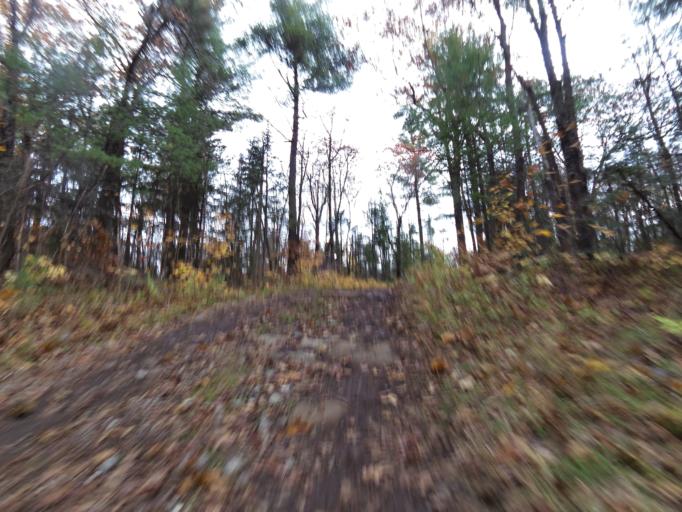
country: CA
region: Quebec
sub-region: Outaouais
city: Wakefield
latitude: 45.5486
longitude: -75.9882
